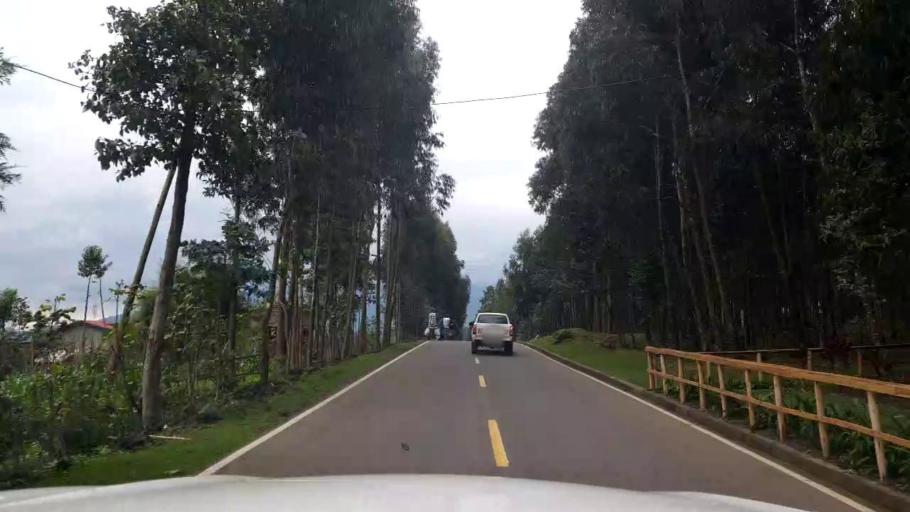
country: RW
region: Northern Province
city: Musanze
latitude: -1.4340
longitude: 29.5569
